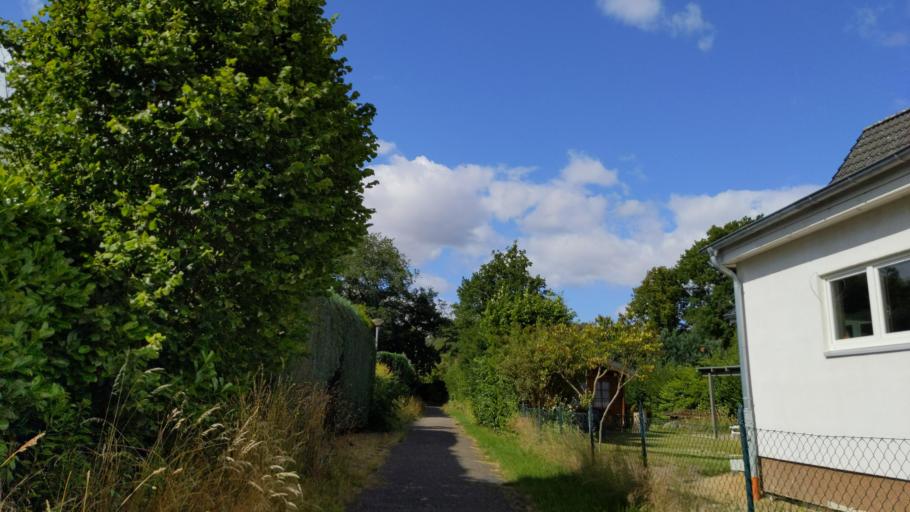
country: DE
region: Schleswig-Holstein
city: Bad Schwartau
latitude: 53.8947
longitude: 10.7146
